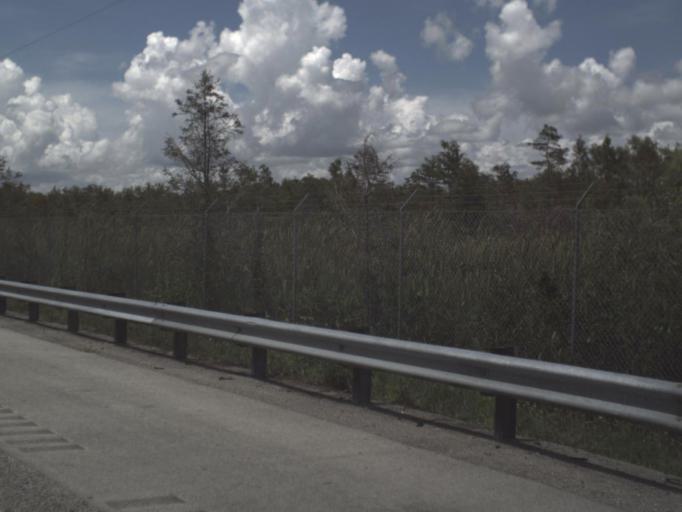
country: US
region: Florida
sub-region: Collier County
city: Immokalee
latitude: 26.1679
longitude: -81.1483
